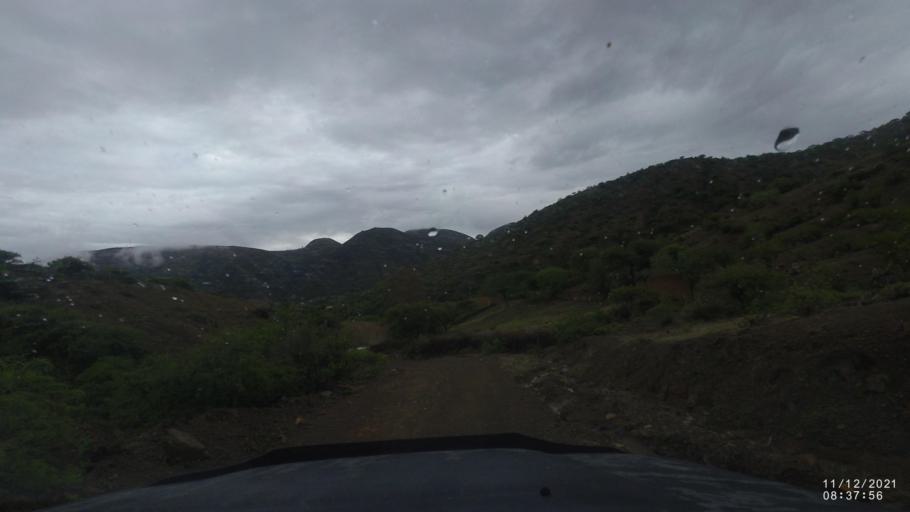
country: BO
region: Cochabamba
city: Tarata
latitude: -17.9244
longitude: -65.9368
